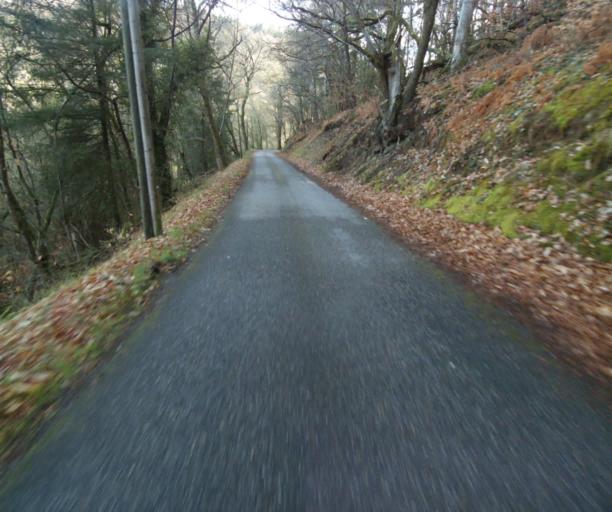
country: FR
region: Limousin
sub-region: Departement de la Correze
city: Correze
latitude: 45.2968
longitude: 1.8475
